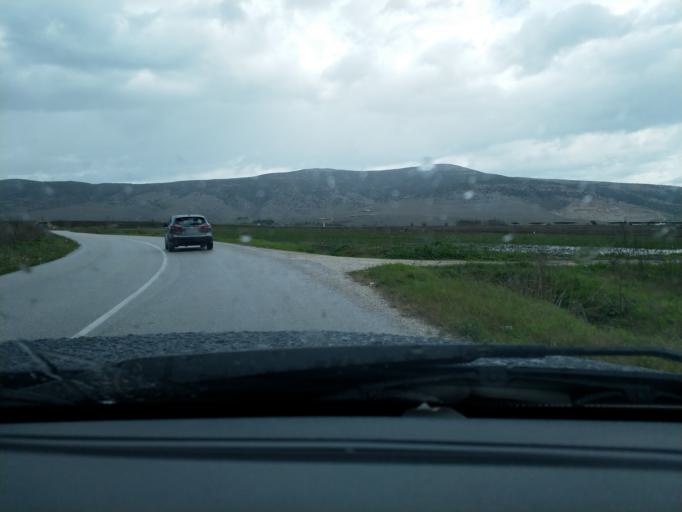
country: GR
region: Thessaly
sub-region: Trikala
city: Taxiarches
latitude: 39.5563
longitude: 21.8902
